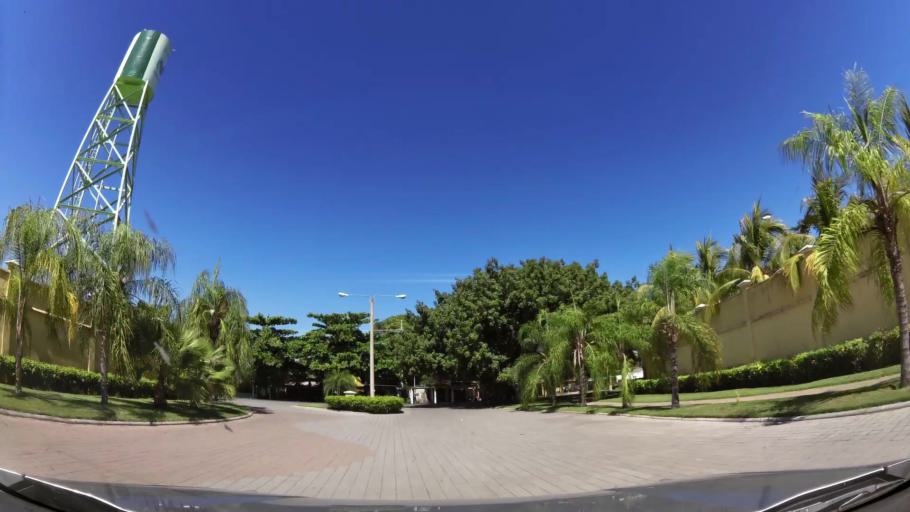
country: GT
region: Escuintla
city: Iztapa
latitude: 13.9394
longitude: -90.7185
